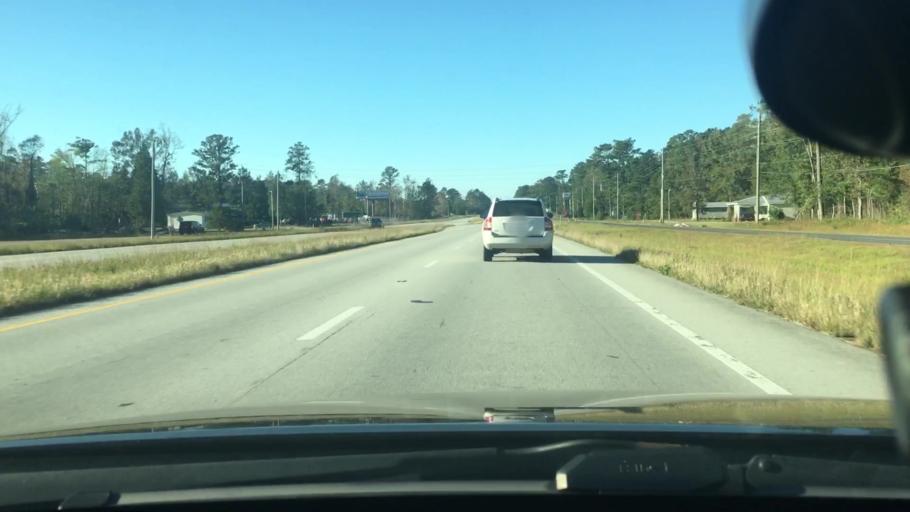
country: US
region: North Carolina
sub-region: Craven County
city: Neuse Forest
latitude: 35.0076
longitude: -76.9905
